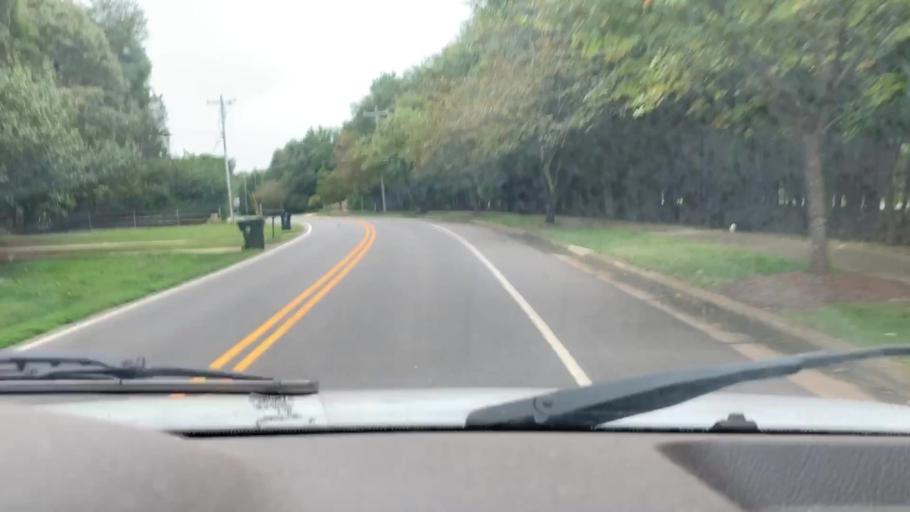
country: US
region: North Carolina
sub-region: Mecklenburg County
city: Cornelius
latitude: 35.4857
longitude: -80.9018
